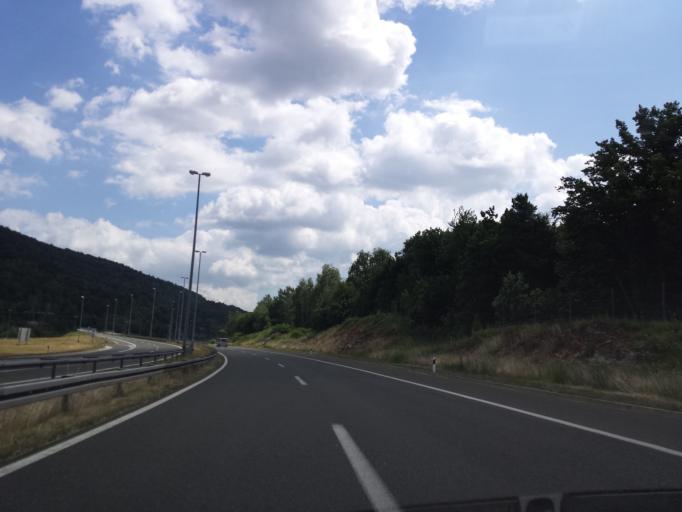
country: HR
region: Karlovacka
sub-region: Grad Ogulin
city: Ogulin
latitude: 45.4060
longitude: 15.2526
